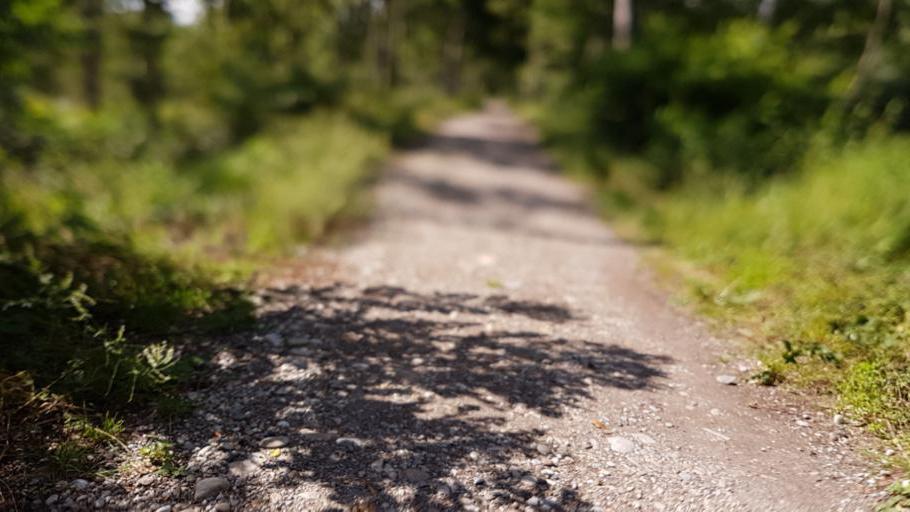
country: CH
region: Bern
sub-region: Bern-Mittelland District
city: Muri
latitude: 46.9163
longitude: 7.5027
